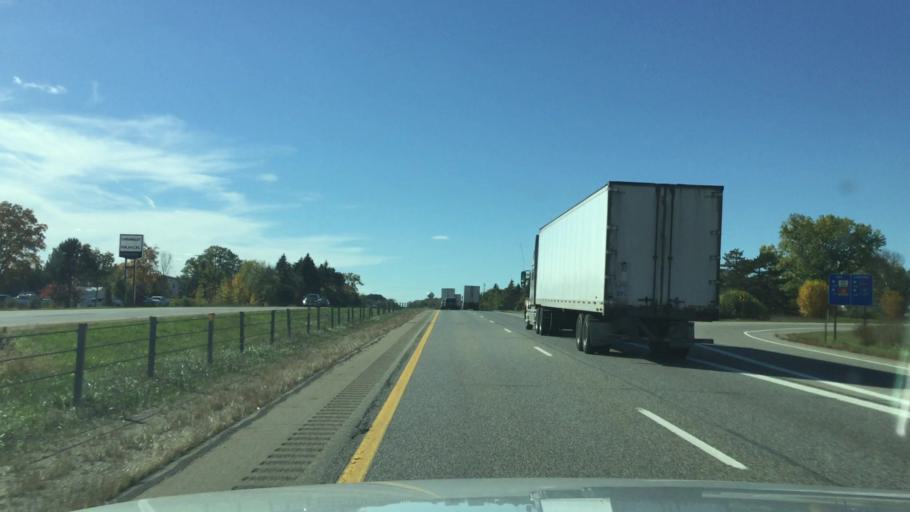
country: US
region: Michigan
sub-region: Washtenaw County
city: Chelsea
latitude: 42.2947
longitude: -84.0276
